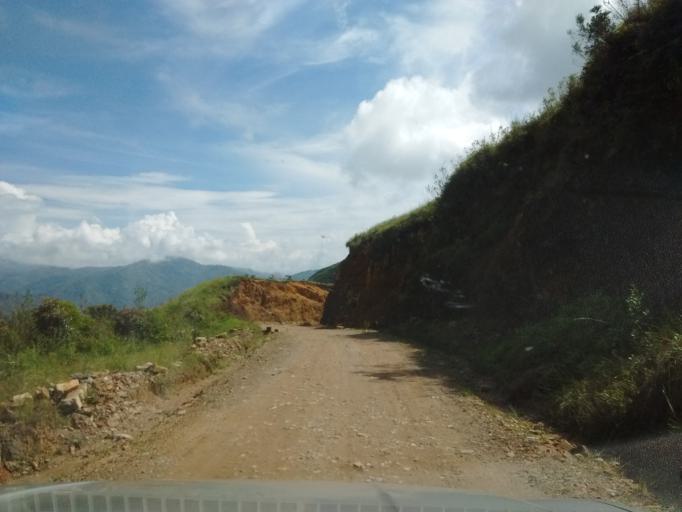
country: CO
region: Cauca
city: Morales
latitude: 2.6906
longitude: -76.7437
